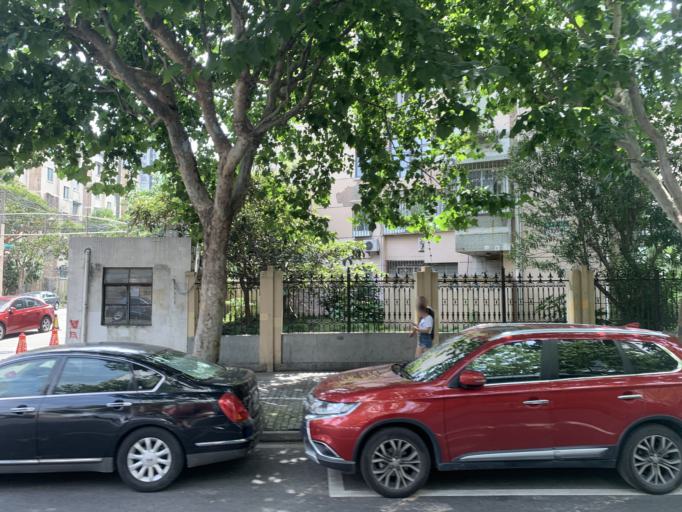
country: CN
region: Shanghai Shi
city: Pudong
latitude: 31.2495
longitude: 121.5594
